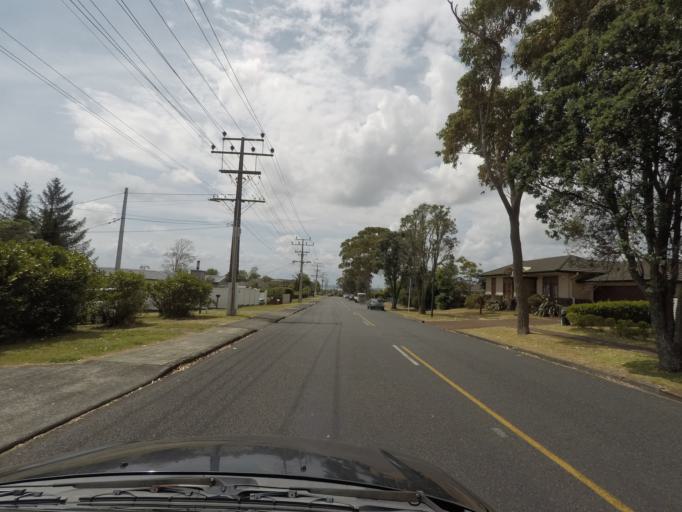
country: NZ
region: Auckland
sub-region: Auckland
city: Waitakere
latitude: -36.9002
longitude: 174.6423
